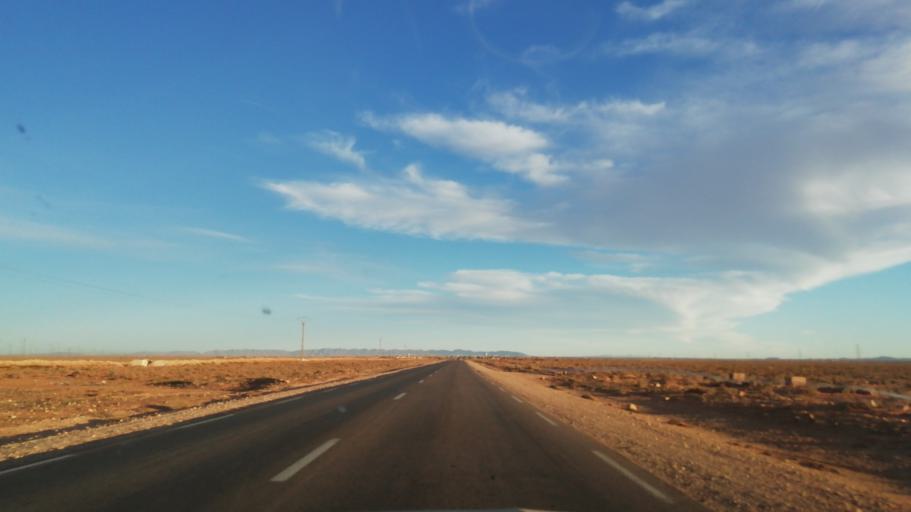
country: DZ
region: Wilaya de Naama
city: Naama
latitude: 33.7349
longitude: -0.7609
